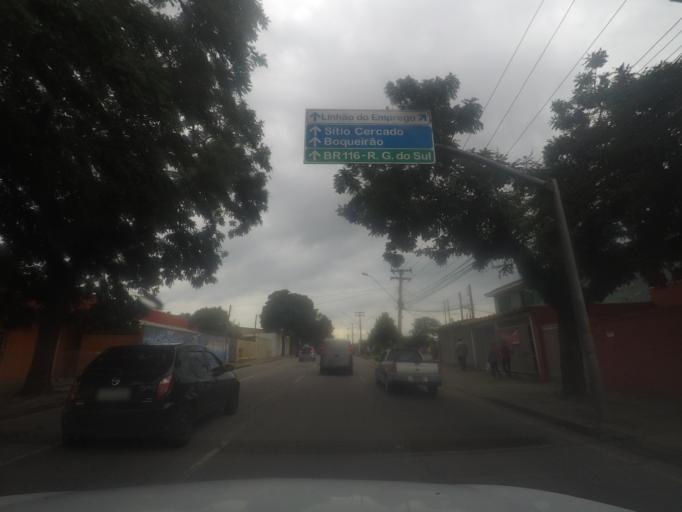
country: BR
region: Parana
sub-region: Sao Jose Dos Pinhais
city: Sao Jose dos Pinhais
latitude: -25.5213
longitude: -49.2971
